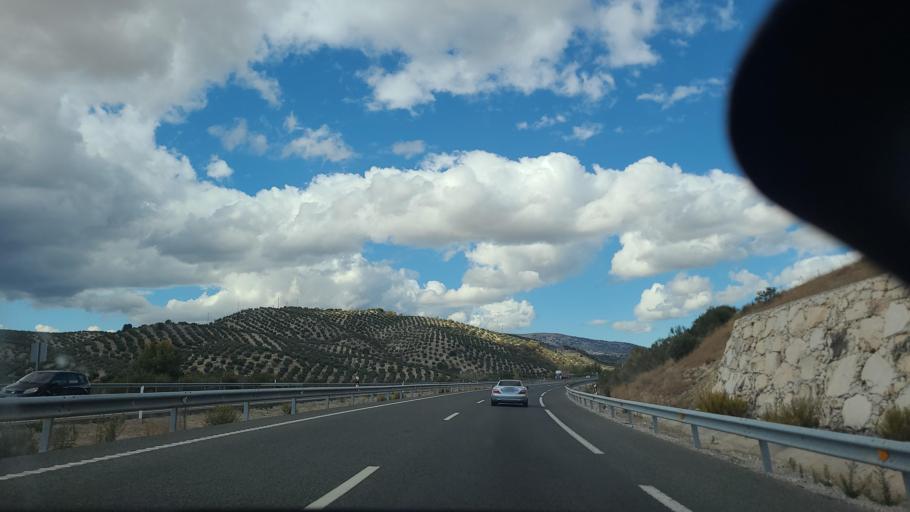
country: ES
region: Andalusia
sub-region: Provincia de Granada
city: Campotejar
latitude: 37.4911
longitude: -3.6218
